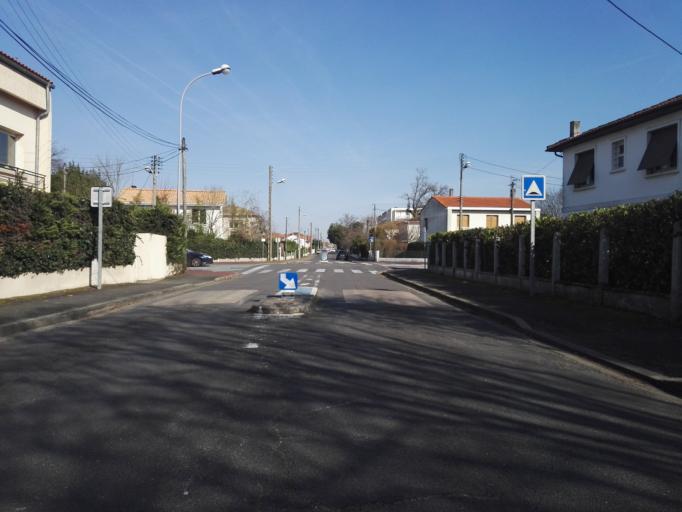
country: FR
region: Aquitaine
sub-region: Departement de la Gironde
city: Talence
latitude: 44.7967
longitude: -0.5882
